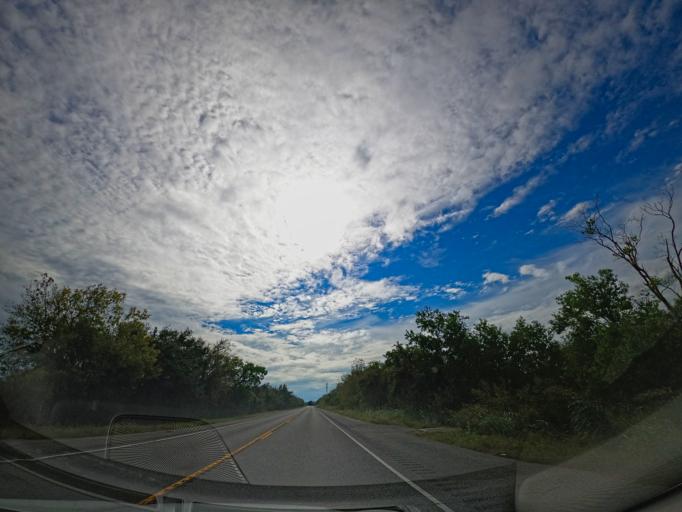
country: US
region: Louisiana
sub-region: Saint Tammany Parish
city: Eden Isle
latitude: 30.0735
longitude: -89.7974
